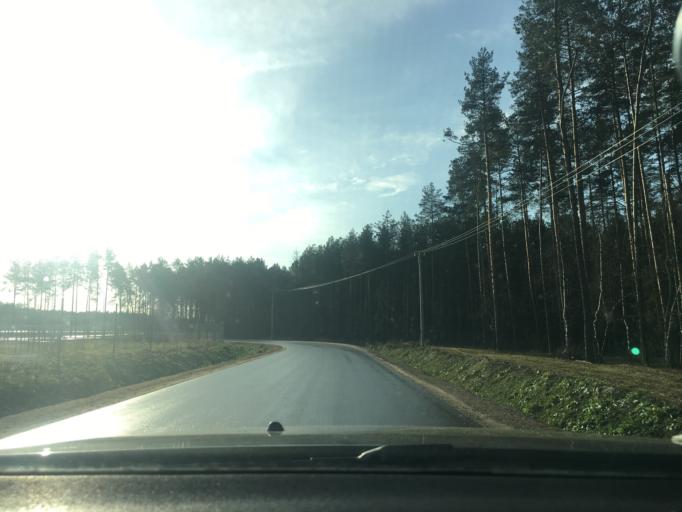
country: PL
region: Swietokrzyskie
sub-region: Powiat jedrzejowski
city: Jedrzejow
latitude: 50.6829
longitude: 20.3527
